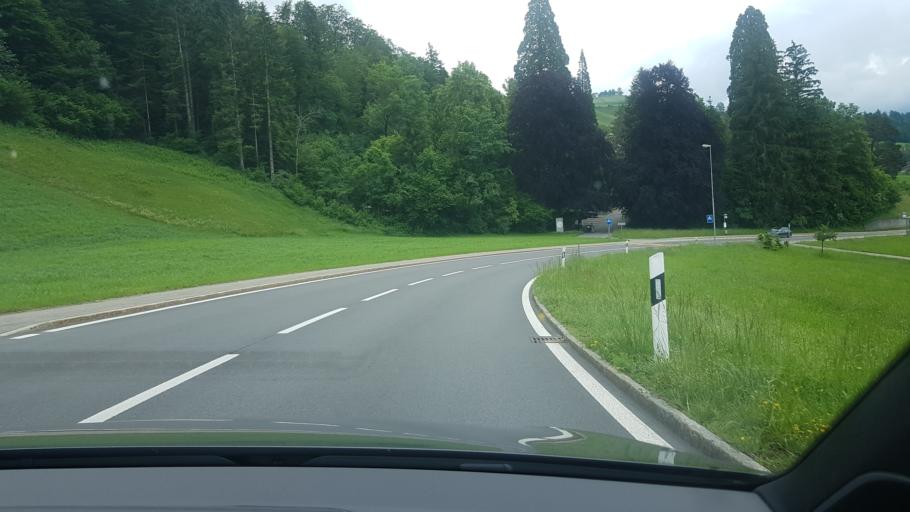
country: CH
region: Zug
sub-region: Zug
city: Menzingen
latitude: 47.1776
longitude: 8.5644
